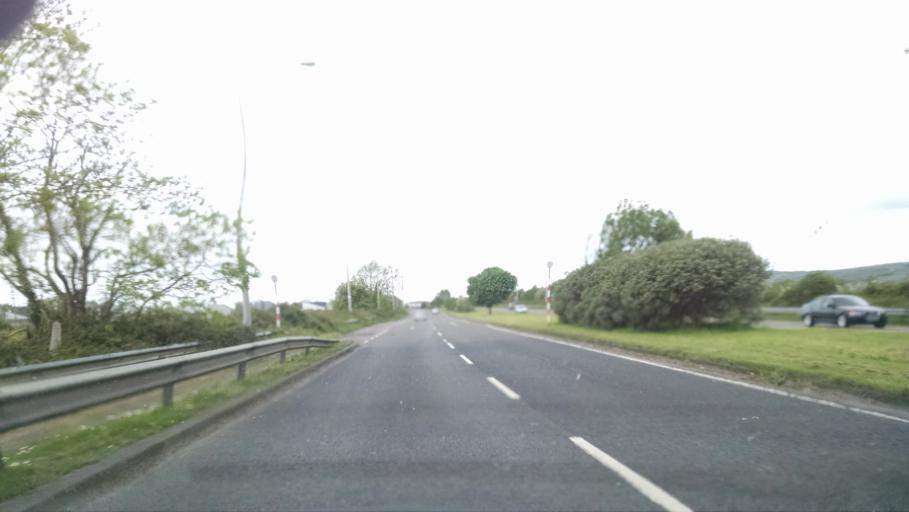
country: IE
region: Munster
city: Moyross
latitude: 52.6767
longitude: -8.6836
